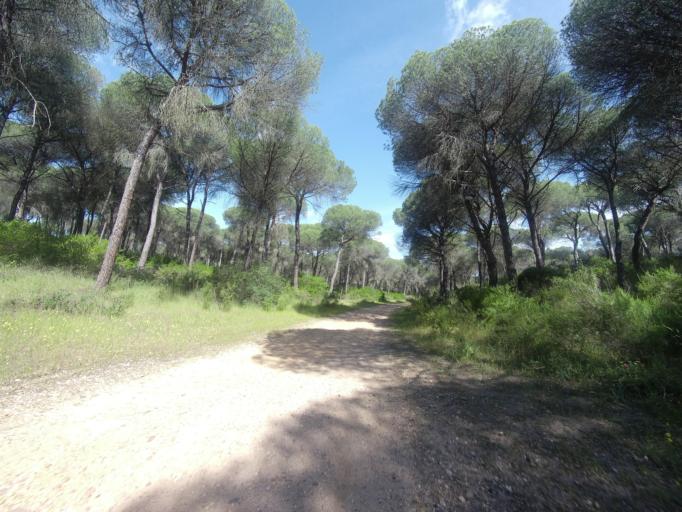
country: ES
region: Andalusia
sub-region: Provincia de Huelva
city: Aljaraque
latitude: 37.2339
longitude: -7.0502
